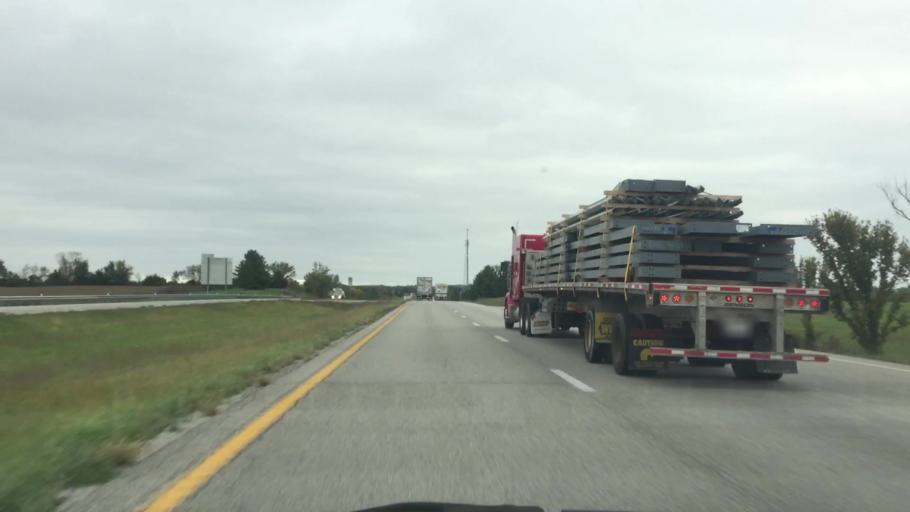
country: US
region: Missouri
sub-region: Clinton County
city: Cameron
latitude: 39.8575
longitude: -94.1749
